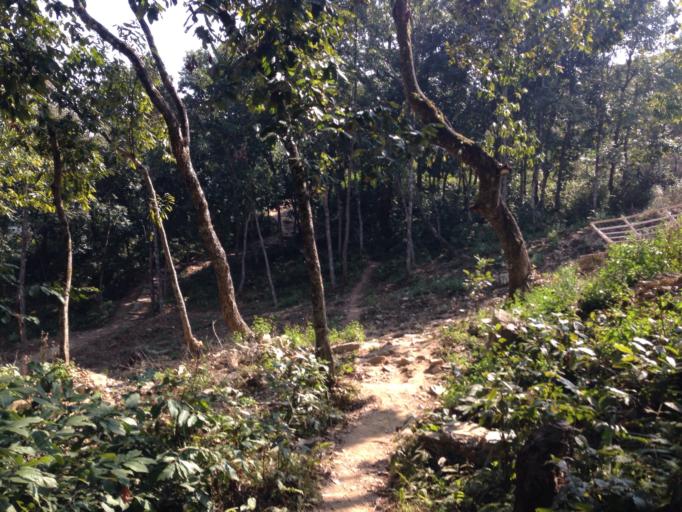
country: NP
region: Western Region
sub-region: Gandaki Zone
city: Pokhara
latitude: 28.2015
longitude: 83.9450
